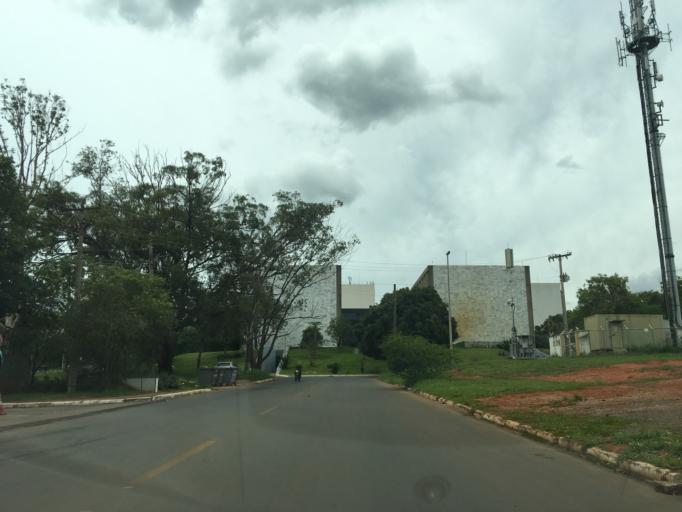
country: BR
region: Federal District
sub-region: Brasilia
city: Brasilia
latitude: -15.7937
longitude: -47.8661
